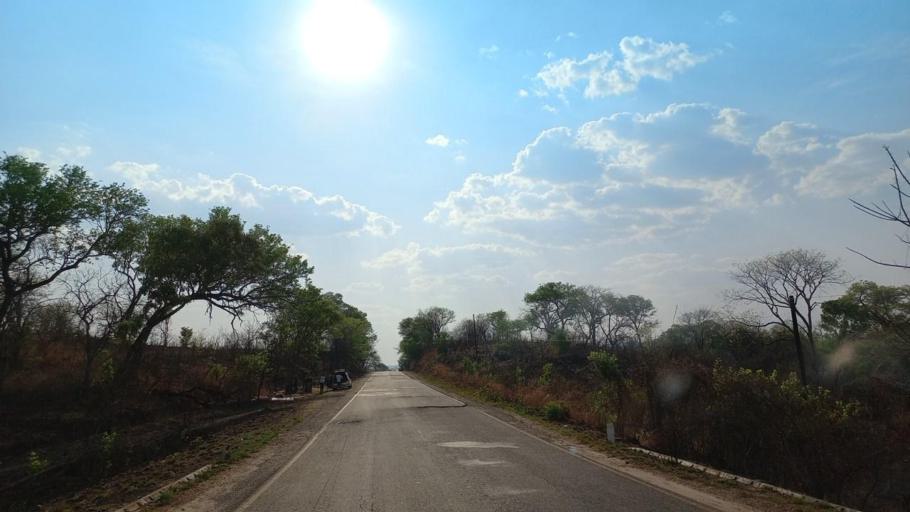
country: ZM
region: Lusaka
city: Luangwa
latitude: -14.9816
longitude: 30.1425
